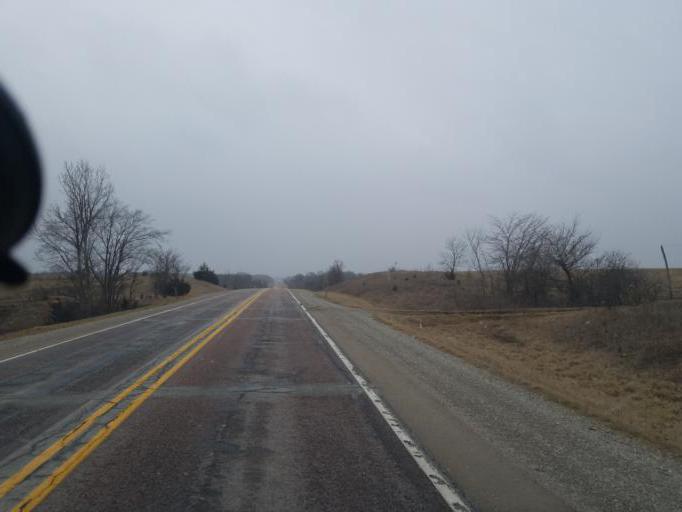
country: US
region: Iowa
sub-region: Appanoose County
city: Centerville
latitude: 40.6215
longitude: -92.9513
